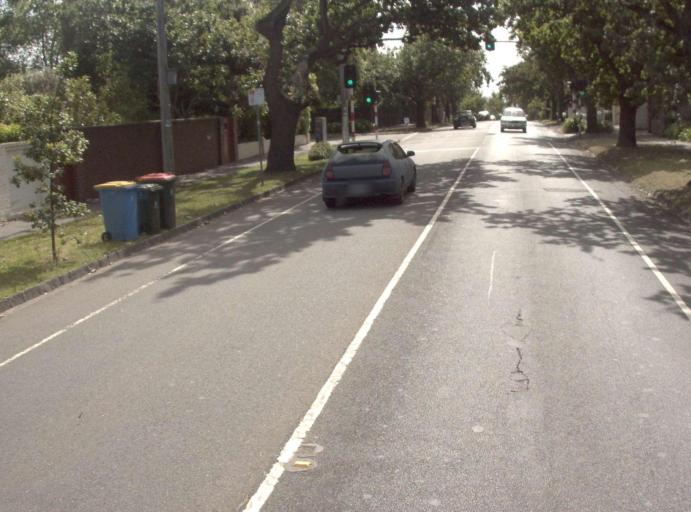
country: AU
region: Victoria
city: Balwyn
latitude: -37.8220
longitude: 145.0637
